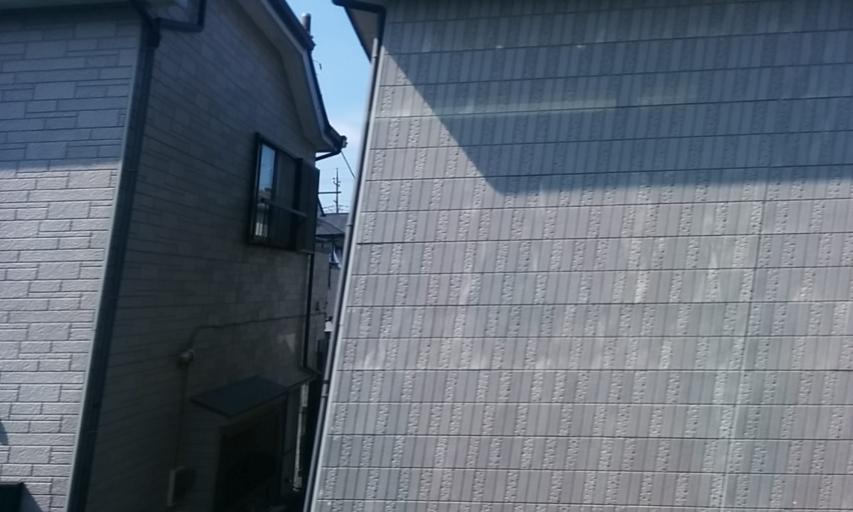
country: JP
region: Saitama
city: Kazo
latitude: 36.1208
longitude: 139.6012
